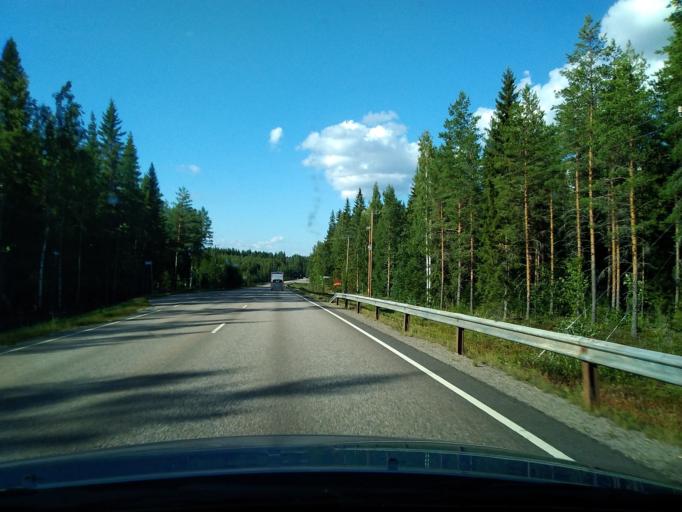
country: FI
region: Pirkanmaa
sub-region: Ylae-Pirkanmaa
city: Maenttae
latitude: 62.0906
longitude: 24.7282
